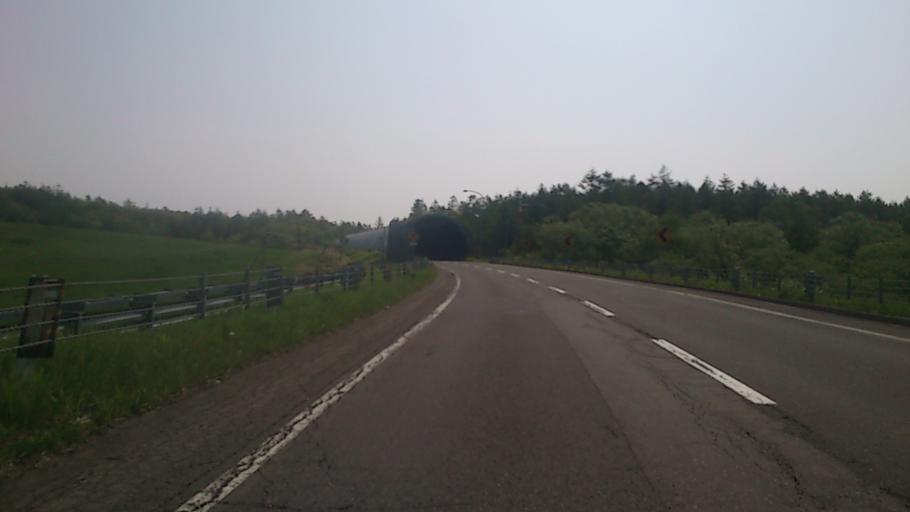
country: JP
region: Hokkaido
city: Kushiro
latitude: 43.4821
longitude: 144.5410
